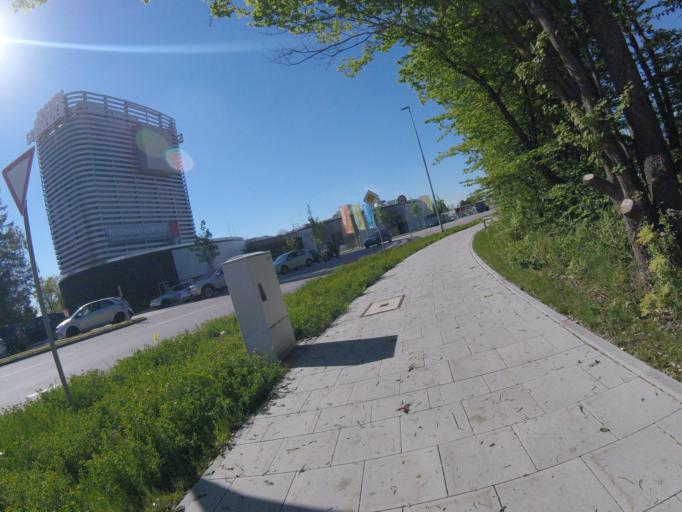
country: DE
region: Bavaria
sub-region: Upper Bavaria
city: Ottobrunn
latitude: 48.0419
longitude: 11.6545
